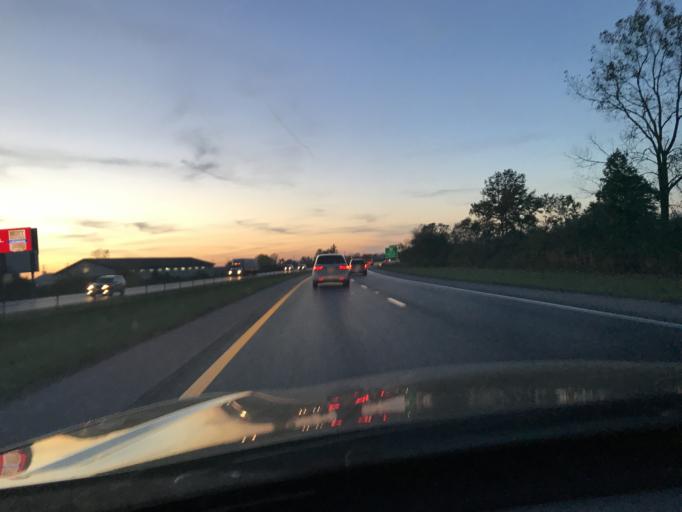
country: US
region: Ohio
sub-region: Franklin County
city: Dublin
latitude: 40.1000
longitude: -83.1700
